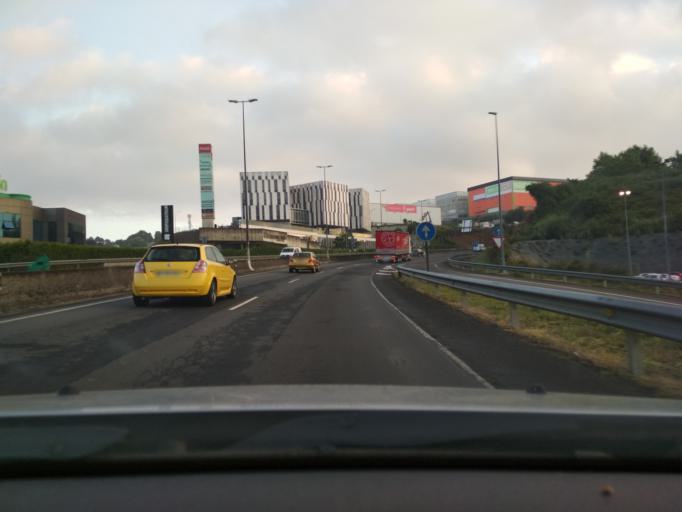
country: ES
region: Galicia
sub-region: Provincia da Coruna
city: Santiago de Compostela
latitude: 42.9030
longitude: -8.5118
